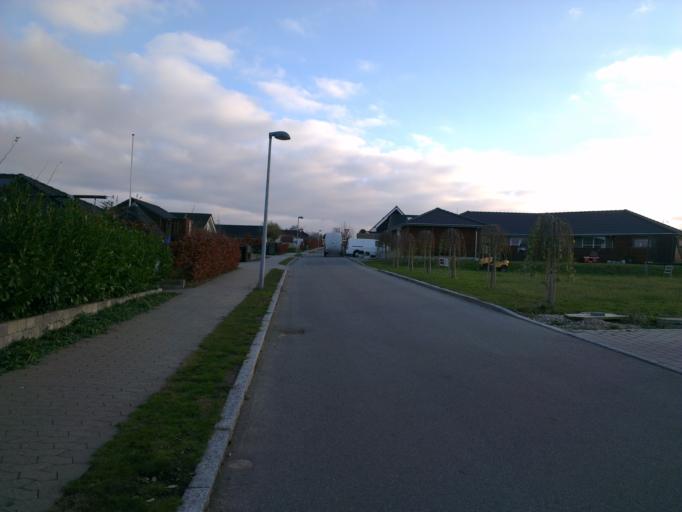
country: DK
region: Capital Region
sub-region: Frederikssund Kommune
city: Jaegerspris
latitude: 55.8479
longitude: 11.9927
